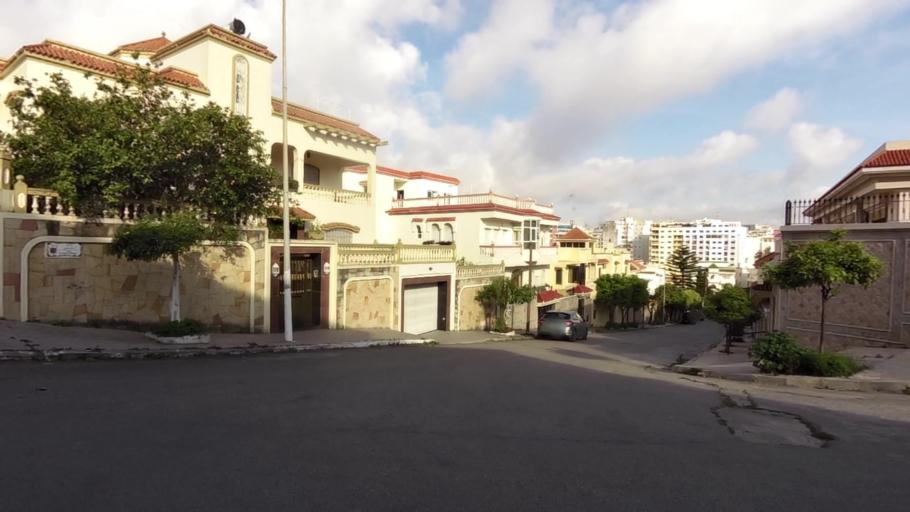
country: MA
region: Tanger-Tetouan
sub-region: Tanger-Assilah
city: Tangier
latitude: 35.7694
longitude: -5.7977
